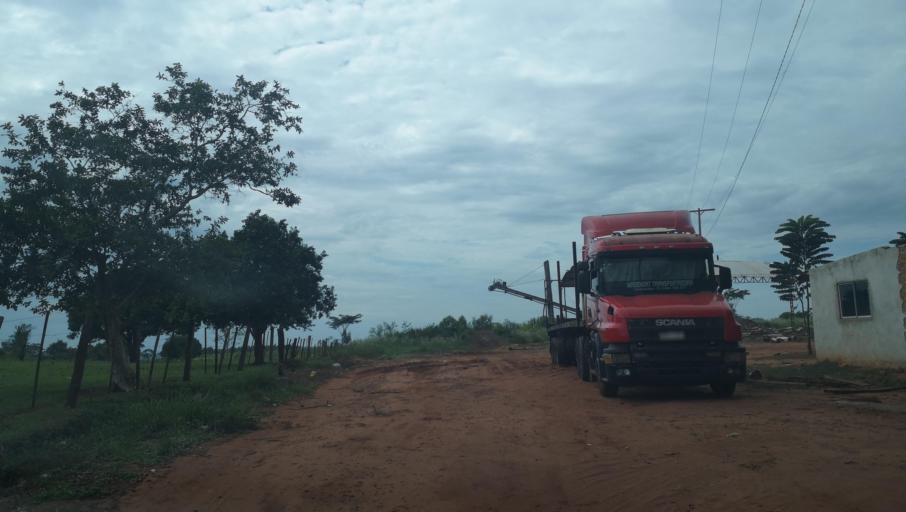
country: PY
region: San Pedro
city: Capiibary
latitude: -24.7149
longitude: -56.0110
